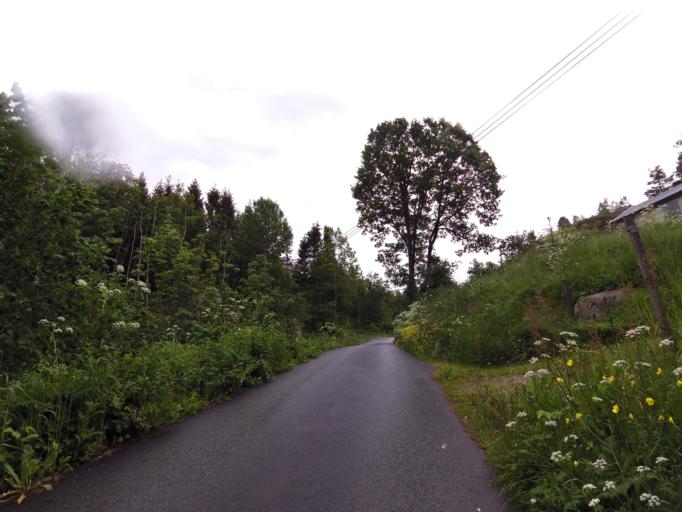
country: NO
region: Vest-Agder
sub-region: Mandal
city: Mandal
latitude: 58.0110
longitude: 7.5121
